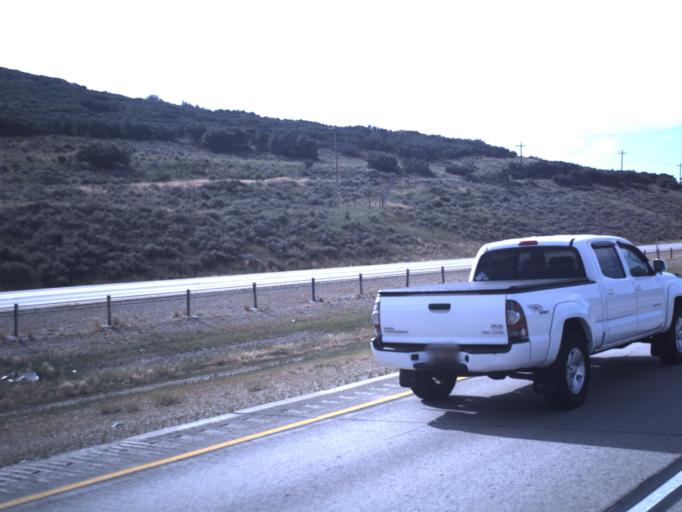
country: US
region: Utah
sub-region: Summit County
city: Park City
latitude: 40.7015
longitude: -111.4744
